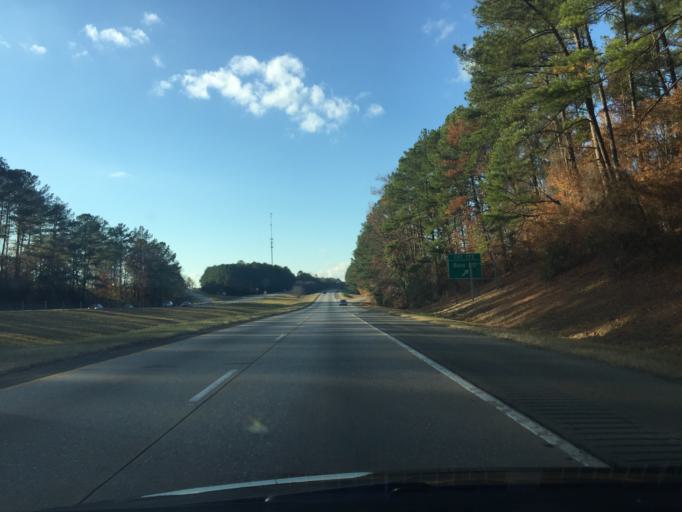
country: US
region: Georgia
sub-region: Bibb County
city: Macon
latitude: 32.9258
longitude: -83.7254
